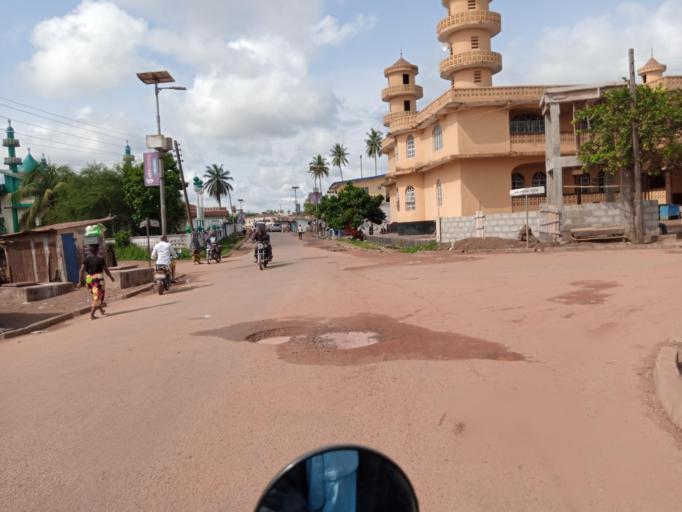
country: SL
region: Southern Province
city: Bo
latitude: 7.9704
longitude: -11.7376
